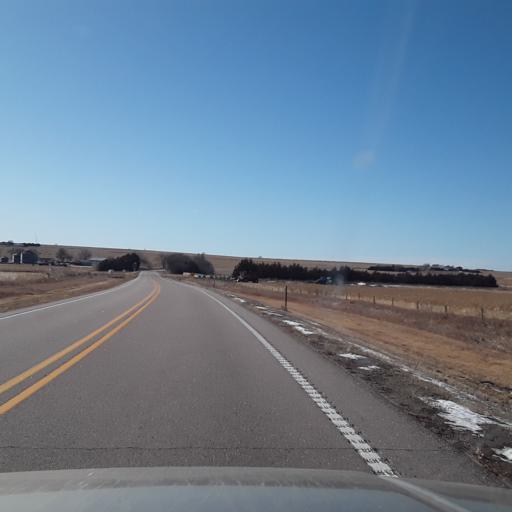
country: US
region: Nebraska
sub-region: Frontier County
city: Stockville
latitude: 40.7045
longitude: -100.2480
